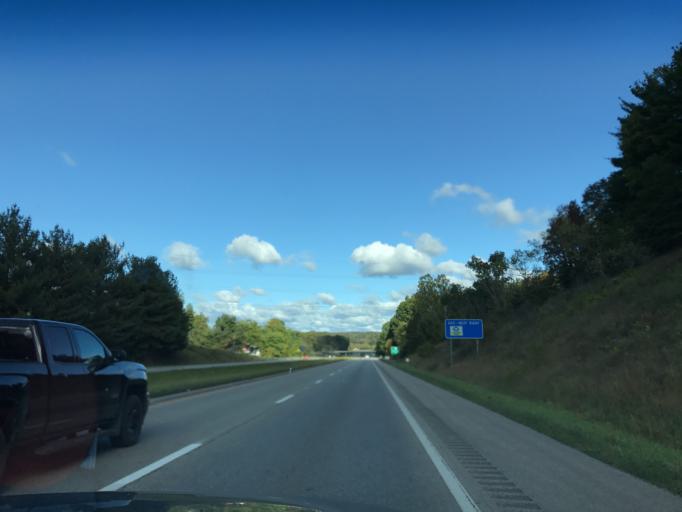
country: US
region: Ohio
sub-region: Athens County
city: The Plains
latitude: 39.3769
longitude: -82.1301
